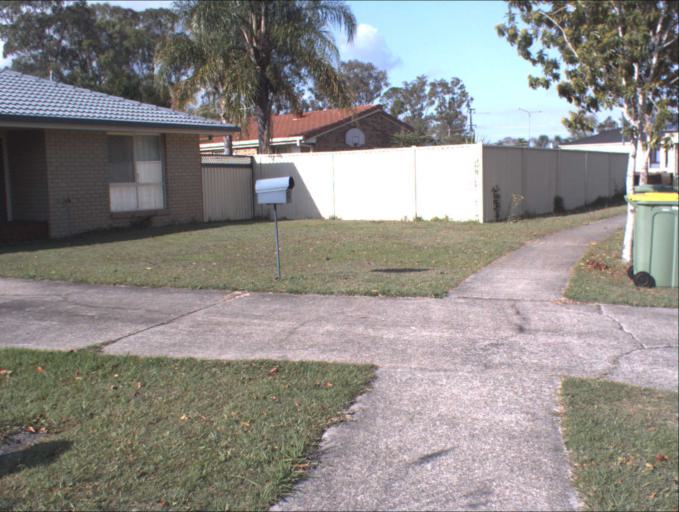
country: AU
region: Queensland
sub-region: Logan
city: Waterford West
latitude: -27.6883
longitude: 153.1259
